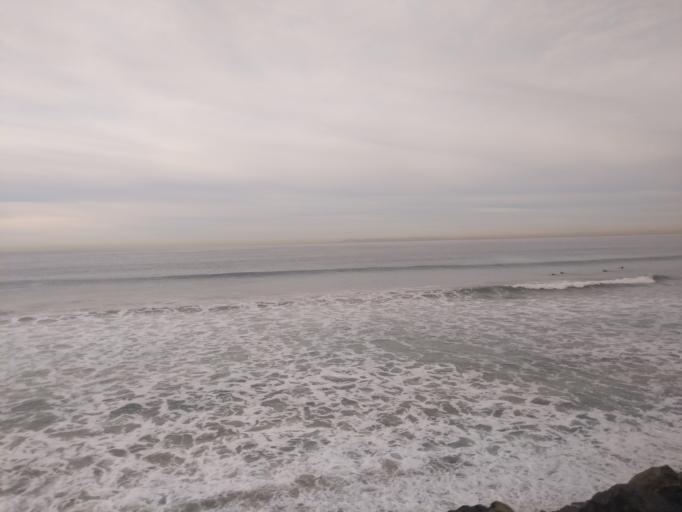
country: US
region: California
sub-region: Orange County
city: San Clemente
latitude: 33.4275
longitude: -117.6287
